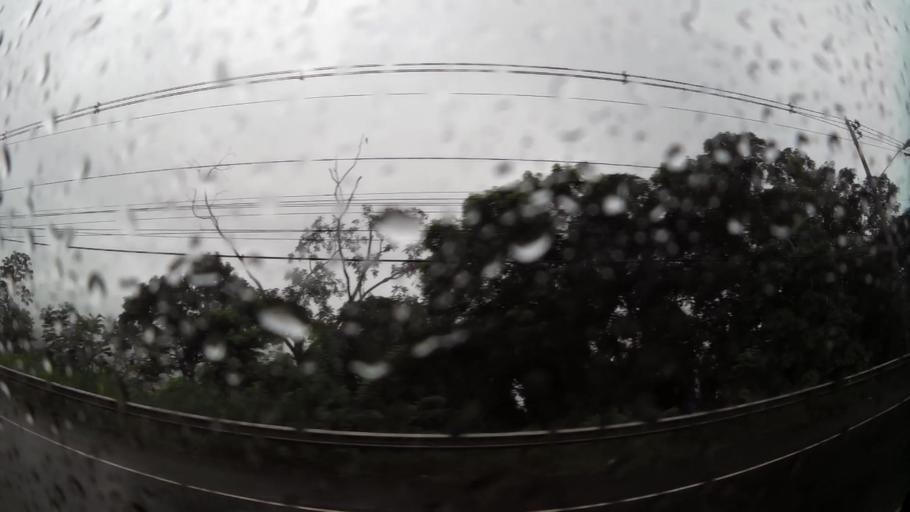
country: PA
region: Colon
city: Gatun
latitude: 9.2847
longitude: -79.7400
